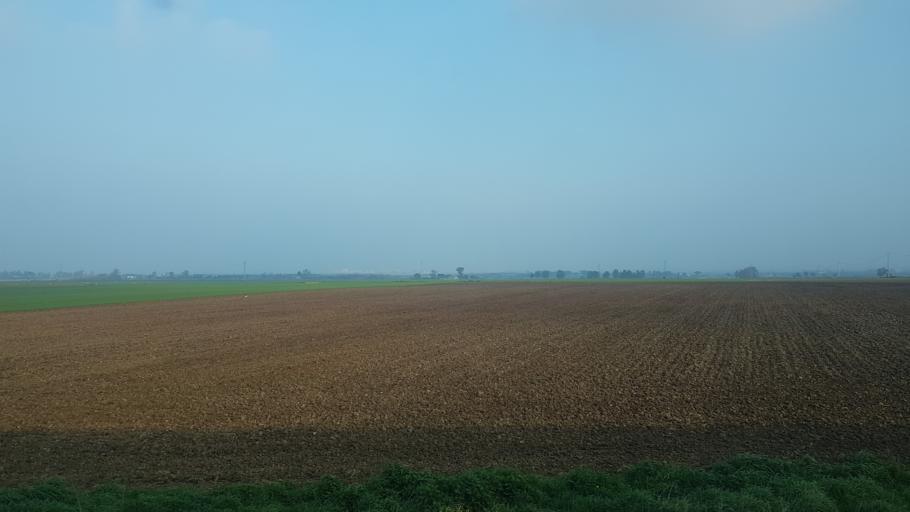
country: IT
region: Apulia
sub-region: Provincia di Foggia
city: Lesina
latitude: 41.8593
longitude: 15.2959
